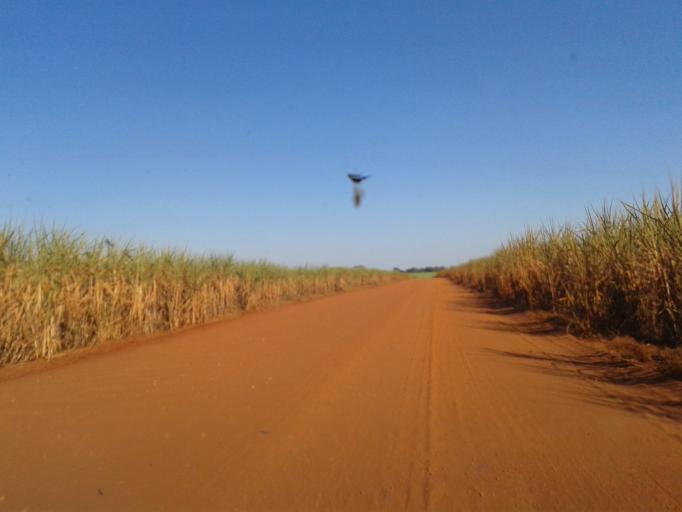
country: BR
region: Minas Gerais
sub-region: Santa Vitoria
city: Santa Vitoria
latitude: -18.8600
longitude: -50.0513
